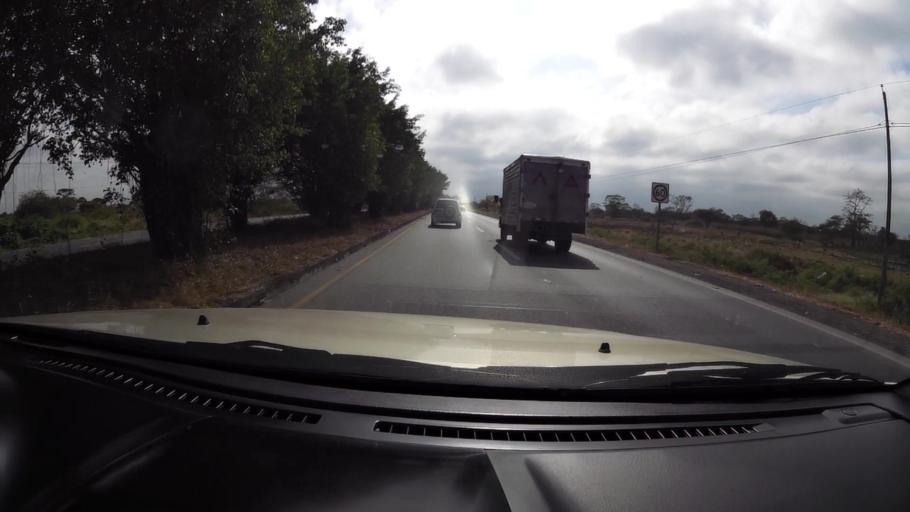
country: EC
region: Guayas
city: Eloy Alfaro
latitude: -2.1992
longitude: -79.7682
